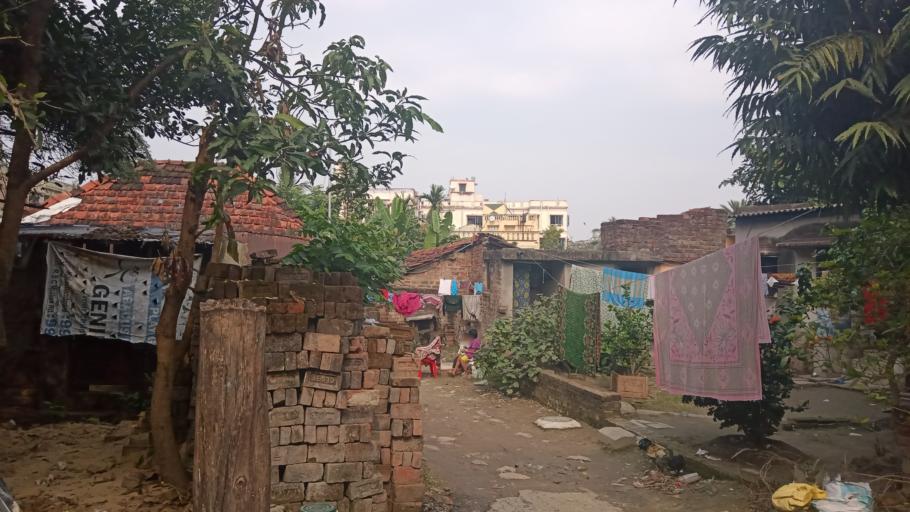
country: IN
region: West Bengal
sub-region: Kolkata
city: Kolkata
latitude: 22.4653
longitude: 88.3831
